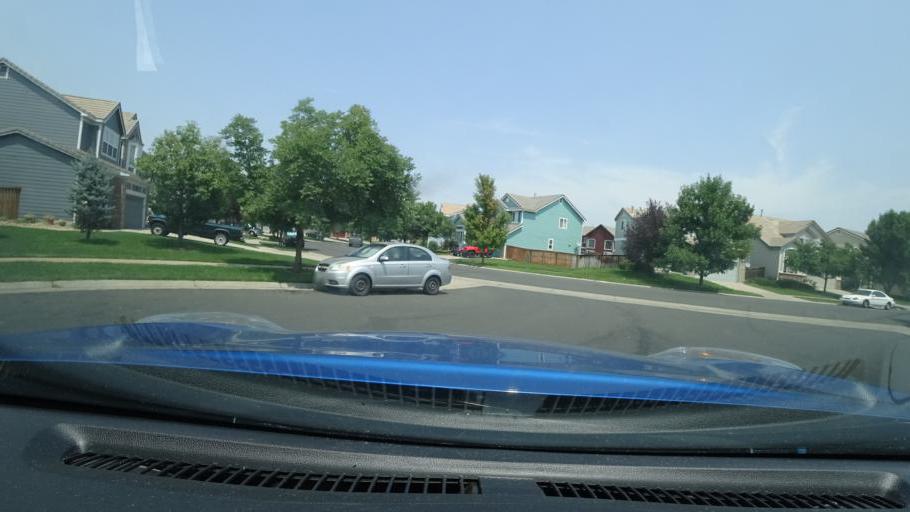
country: US
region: Colorado
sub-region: Adams County
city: Aurora
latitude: 39.7698
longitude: -104.7640
